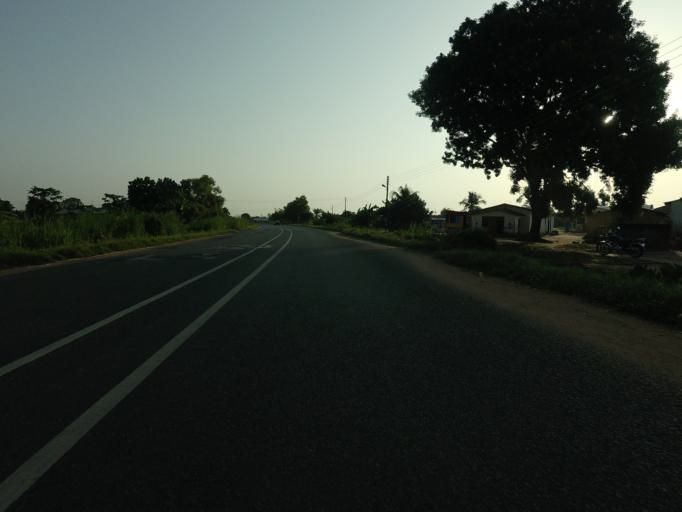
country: GH
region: Volta
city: Anloga
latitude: 5.9802
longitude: 0.6708
